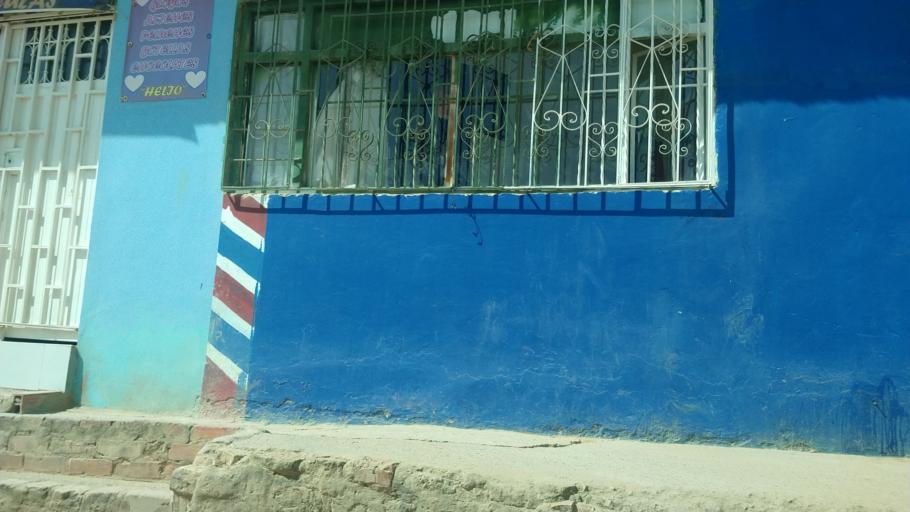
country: CO
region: Cundinamarca
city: Soacha
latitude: 4.5631
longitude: -74.1851
